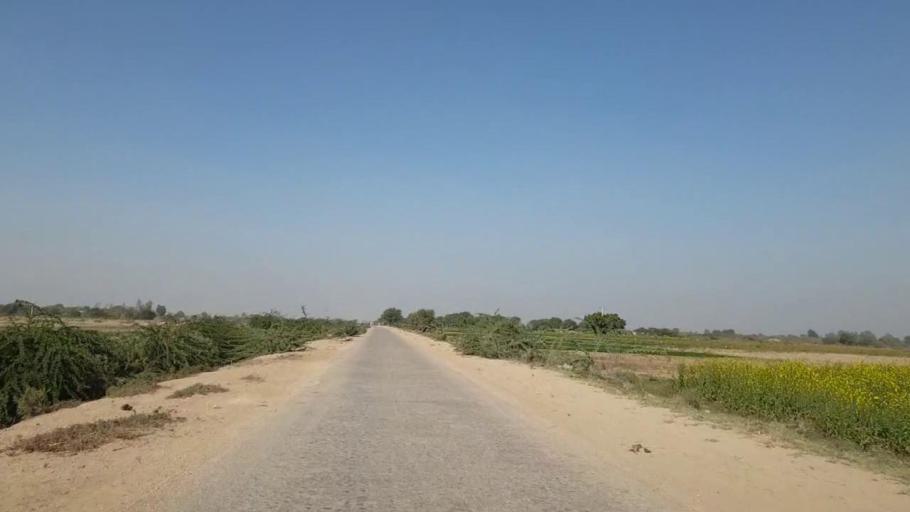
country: PK
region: Sindh
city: Digri
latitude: 25.0182
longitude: 69.1058
